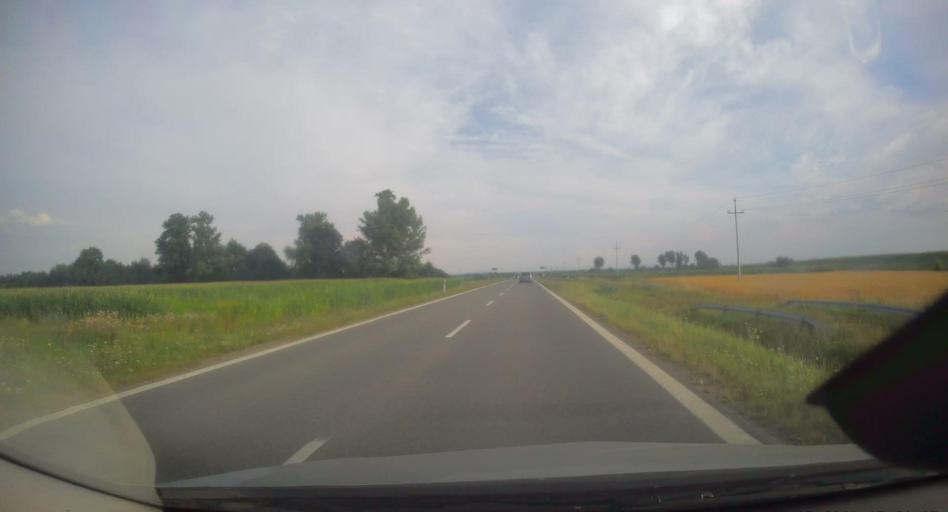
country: PL
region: Lesser Poland Voivodeship
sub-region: Powiat brzeski
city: Szczurowa
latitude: 50.1297
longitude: 20.6123
